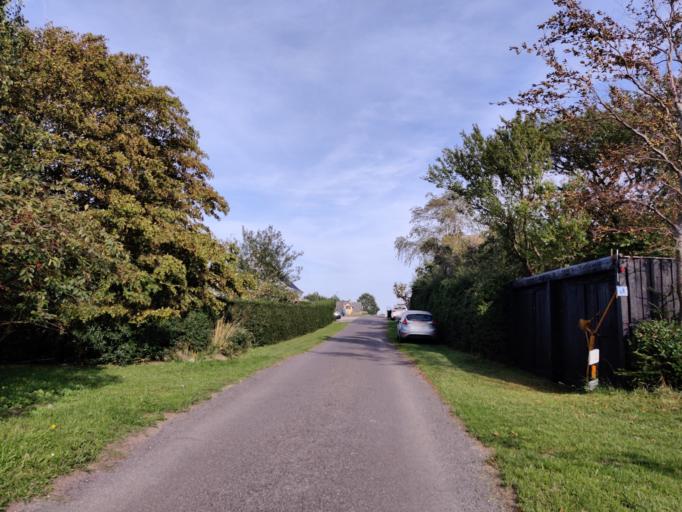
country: DK
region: Zealand
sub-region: Guldborgsund Kommune
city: Nykobing Falster
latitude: 54.6606
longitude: 11.8699
